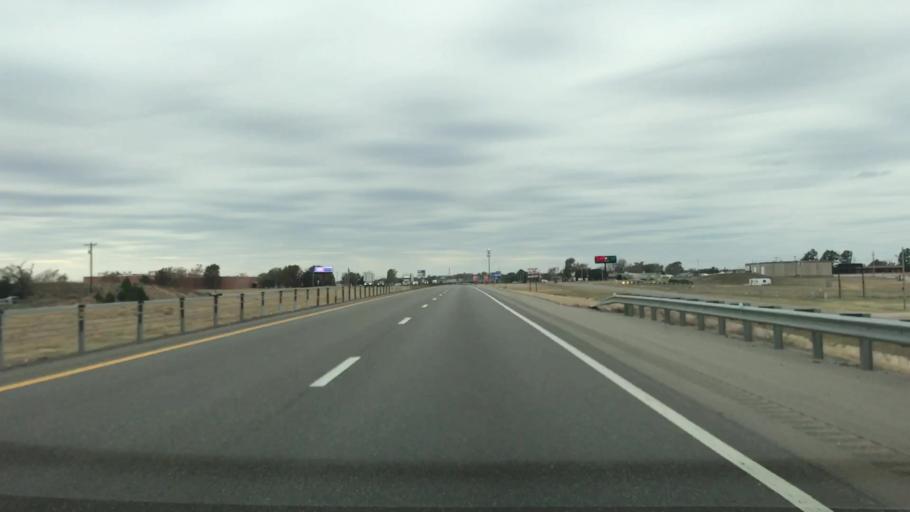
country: US
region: Oklahoma
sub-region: Custer County
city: Weatherford
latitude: 35.5364
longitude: -98.6660
